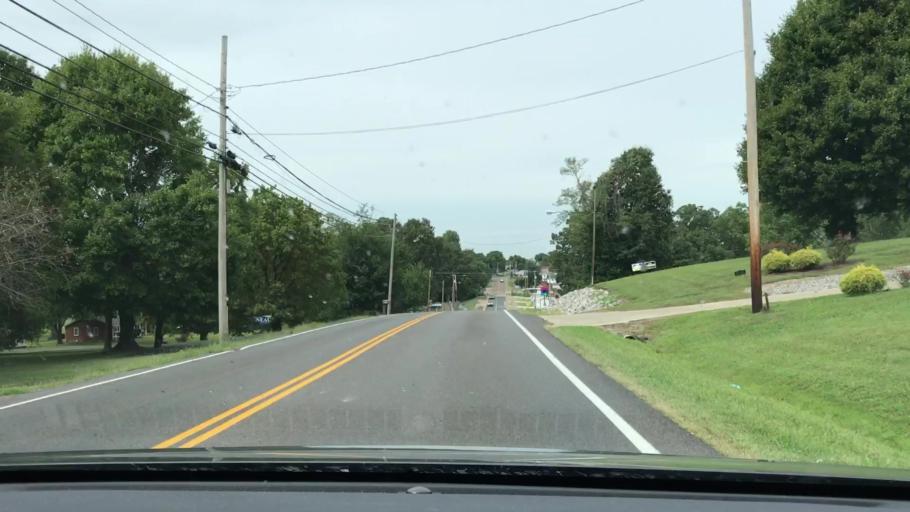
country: US
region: Kentucky
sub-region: Marshall County
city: Benton
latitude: 36.8488
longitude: -88.3502
